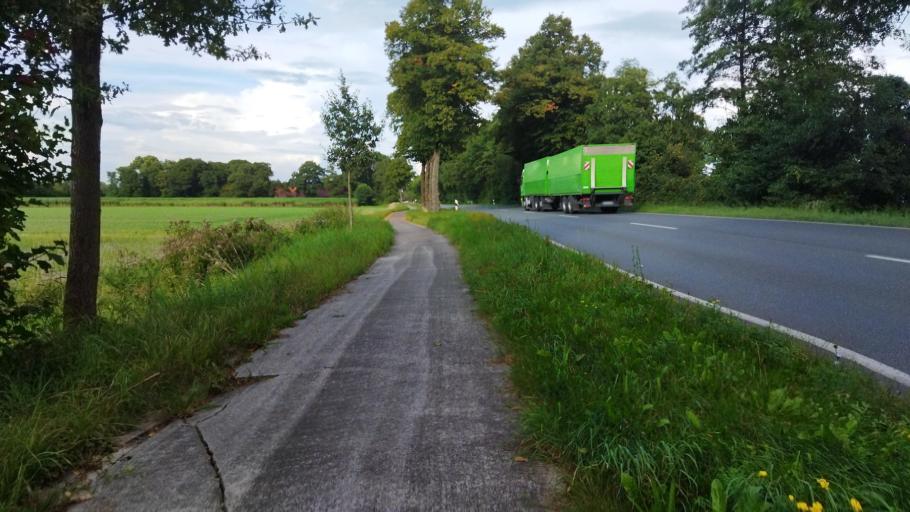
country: DE
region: Lower Saxony
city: Glandorf
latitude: 52.0664
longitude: 7.9572
